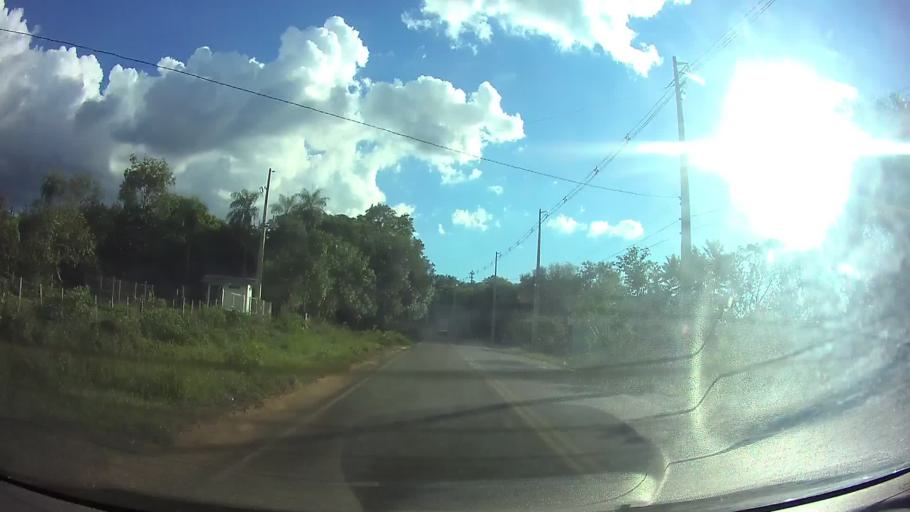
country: PY
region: Cordillera
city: Altos
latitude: -25.2460
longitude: -57.2340
